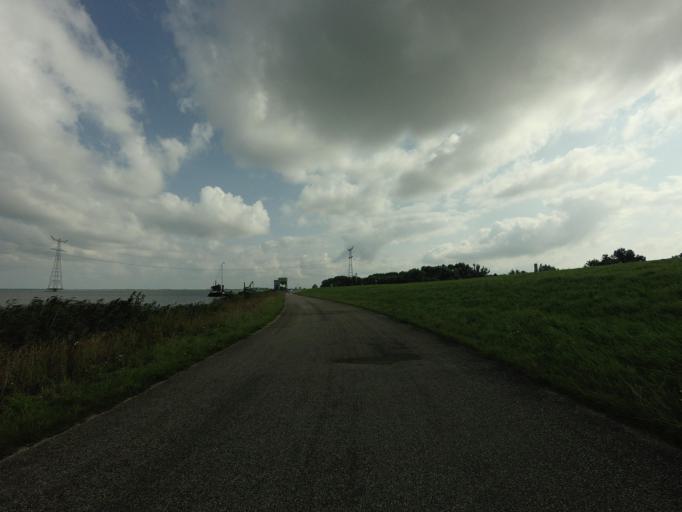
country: NL
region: Flevoland
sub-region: Gemeente Urk
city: Urk
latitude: 52.6078
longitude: 5.6398
